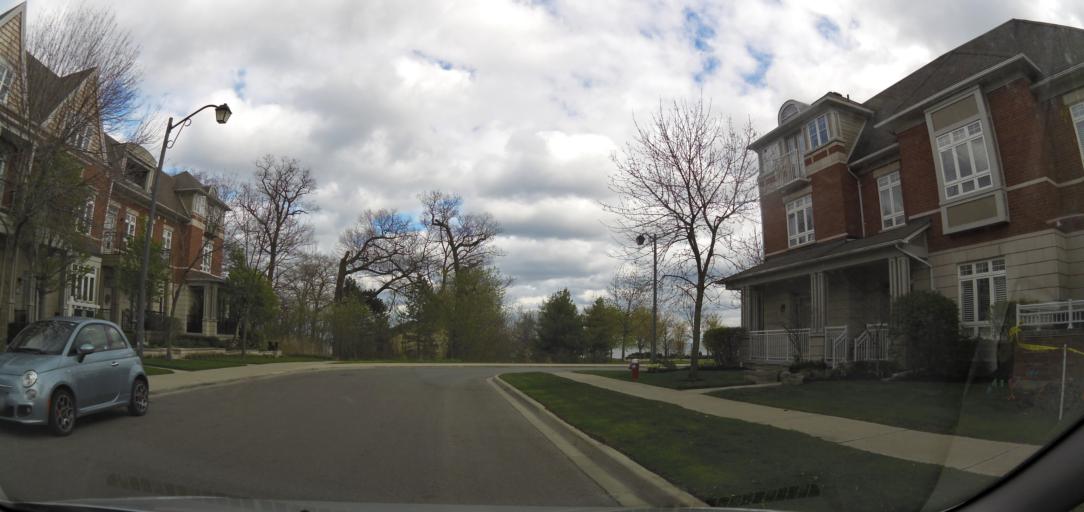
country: CA
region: Ontario
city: Mississauga
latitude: 43.5556
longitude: -79.5781
